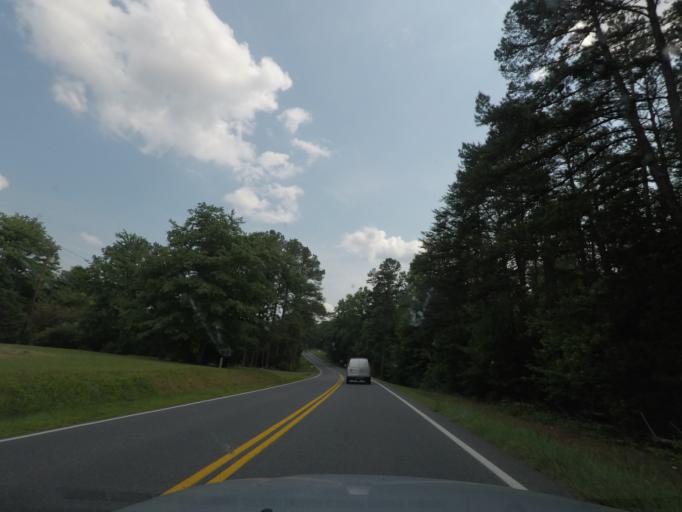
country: US
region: Virginia
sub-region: Fluvanna County
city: Palmyra
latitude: 37.9072
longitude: -78.2573
